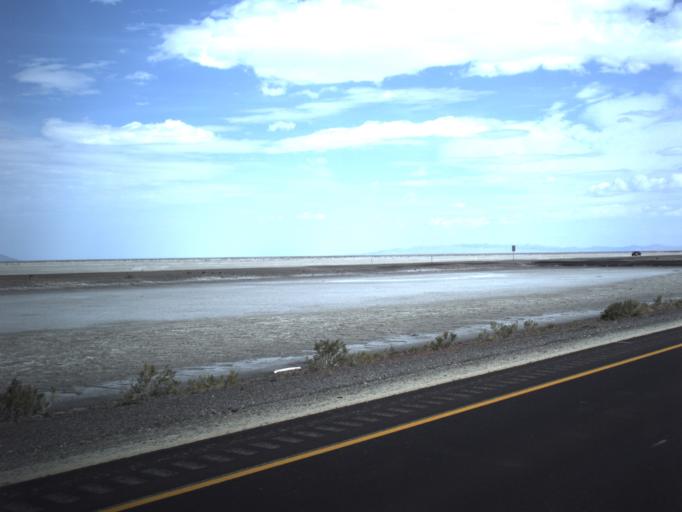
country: US
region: Utah
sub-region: Tooele County
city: Wendover
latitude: 40.7331
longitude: -113.5967
